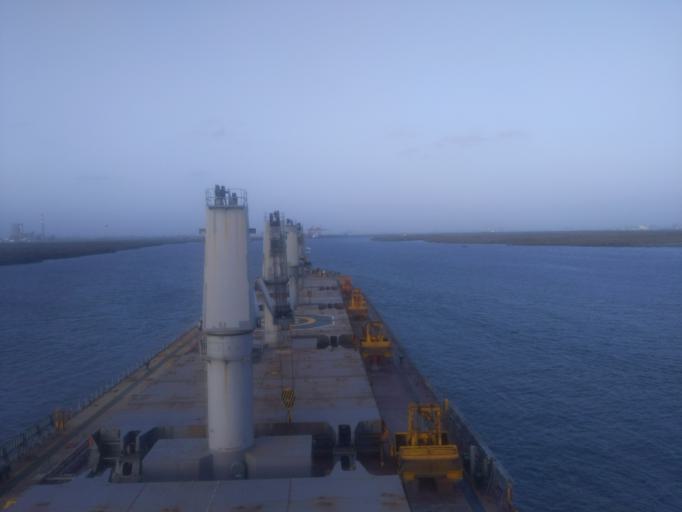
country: PK
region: Sindh
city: Malir Cantonment
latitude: 24.7825
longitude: 67.2432
